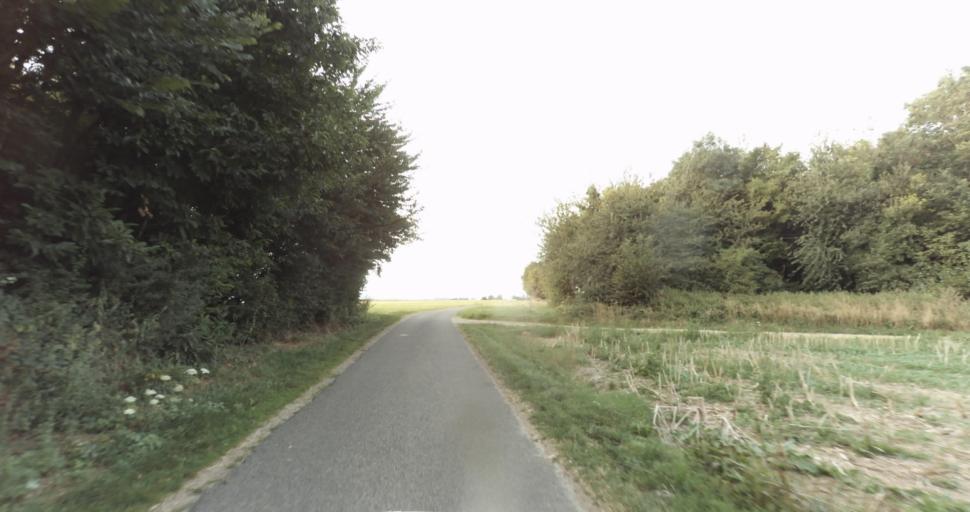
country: FR
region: Haute-Normandie
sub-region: Departement de l'Eure
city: Saint-Germain-sur-Avre
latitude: 48.8385
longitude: 1.2702
